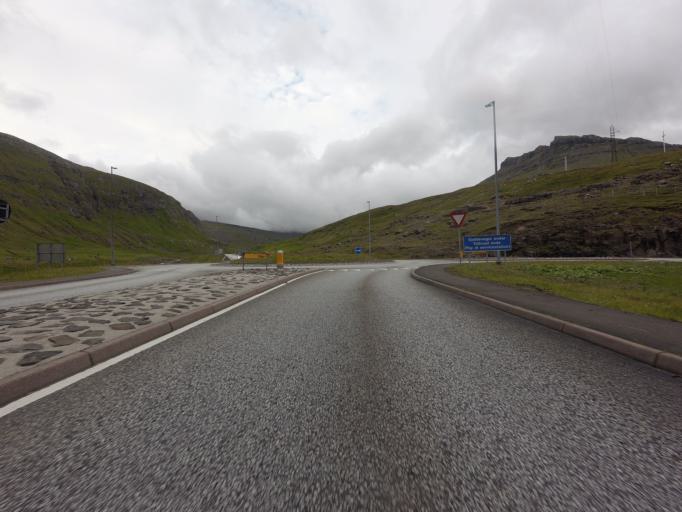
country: FO
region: Streymoy
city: Vestmanna
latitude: 62.1235
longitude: -7.0419
